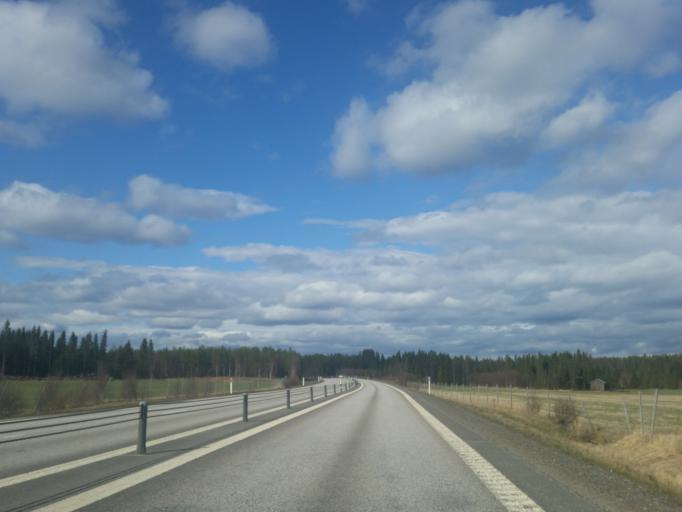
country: SE
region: Vaesterbotten
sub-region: Robertsfors Kommun
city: Robertsfors
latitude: 64.1079
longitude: 20.8763
